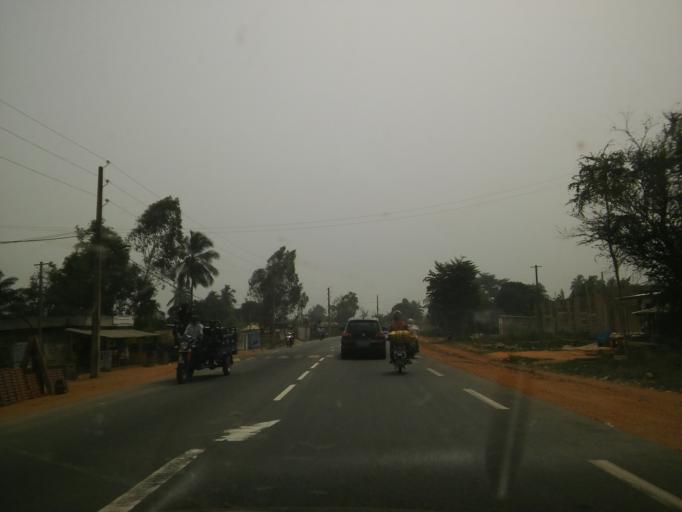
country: BJ
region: Mono
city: Come
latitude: 6.3996
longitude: 1.9223
